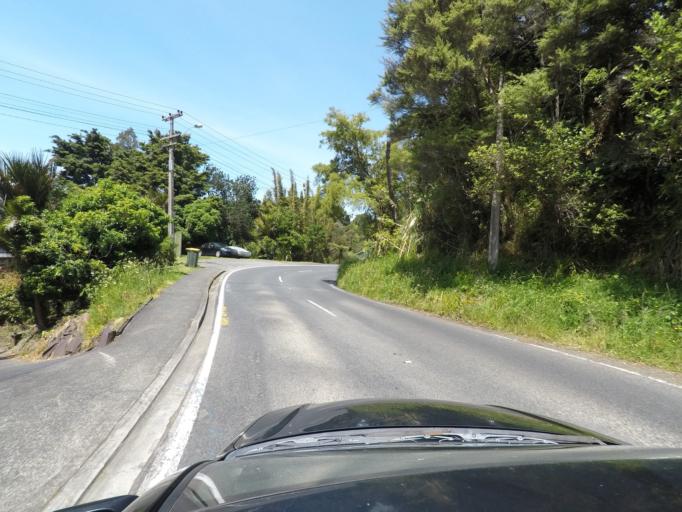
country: NZ
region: Auckland
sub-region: Auckland
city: Titirangi
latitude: -36.9640
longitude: 174.6409
